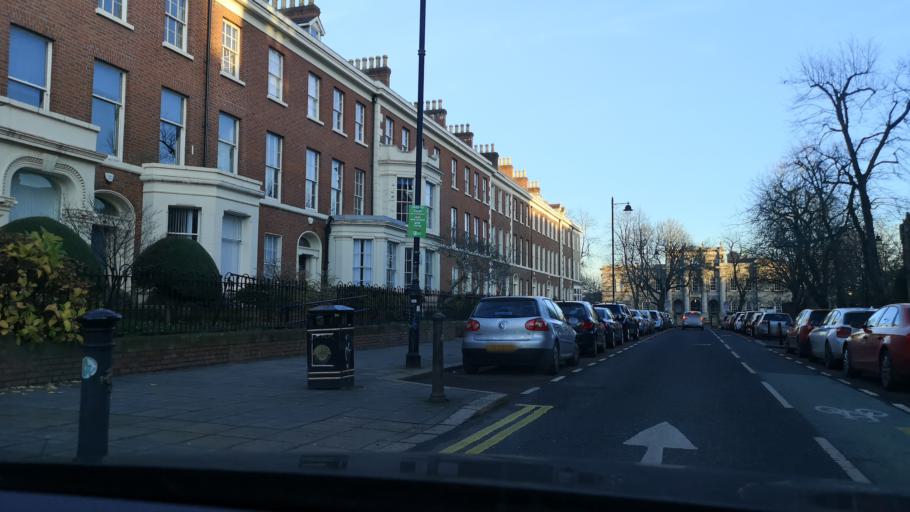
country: GB
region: Northern Ireland
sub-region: City of Belfast
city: Belfast
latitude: 54.5853
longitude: -5.9341
